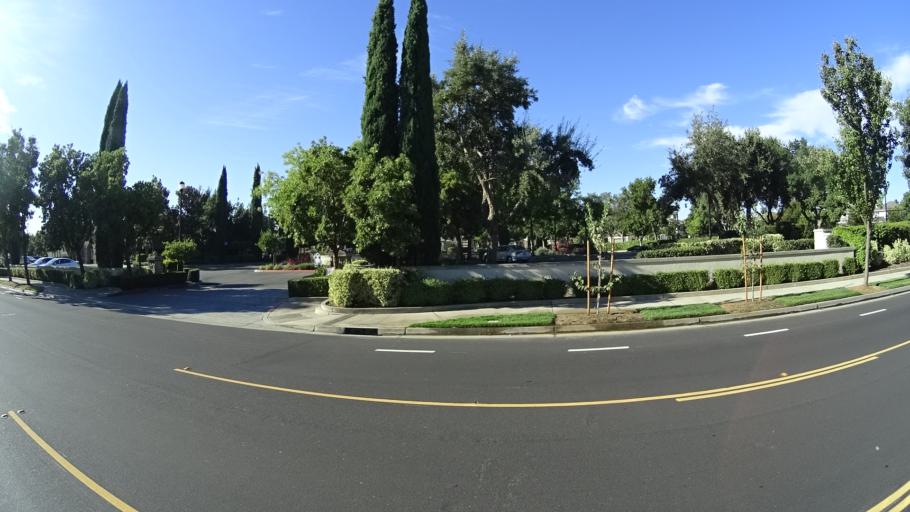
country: US
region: California
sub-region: Sacramento County
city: Laguna
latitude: 38.4036
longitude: -121.4731
